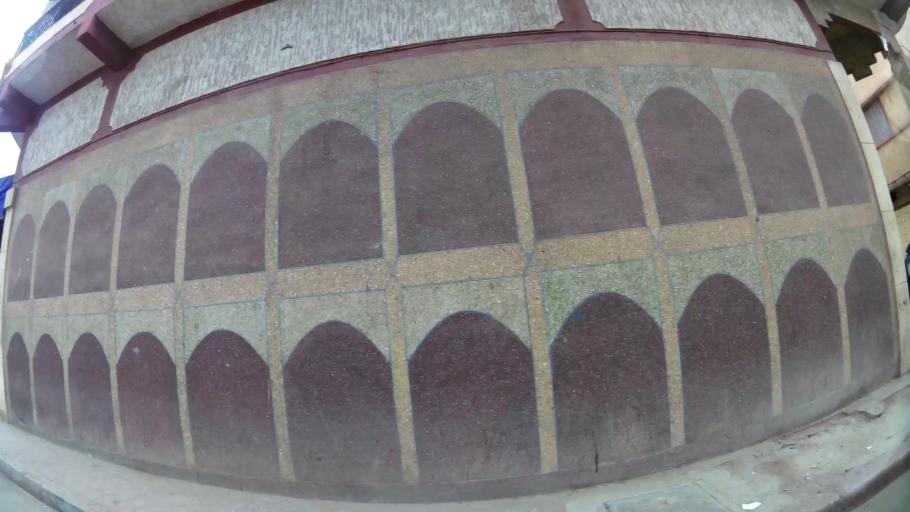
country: MA
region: Rabat-Sale-Zemmour-Zaer
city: Sale
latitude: 34.0519
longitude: -6.7740
